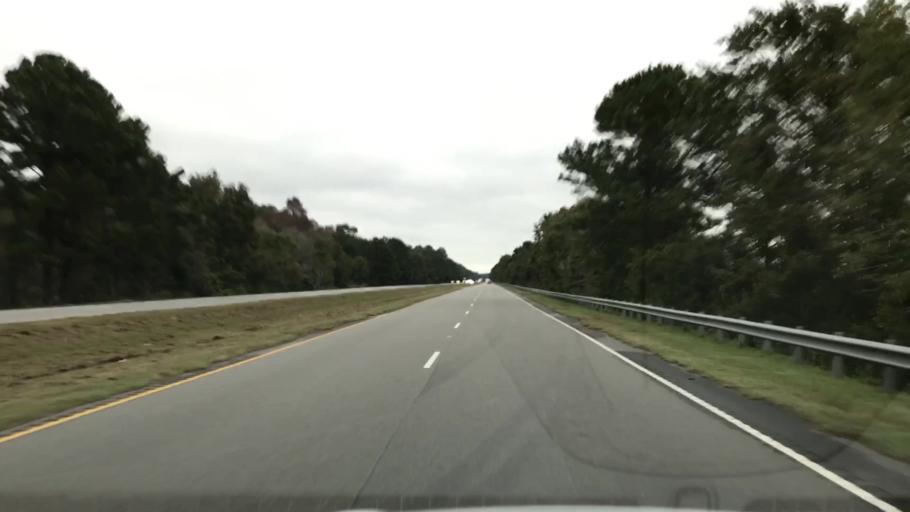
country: US
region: South Carolina
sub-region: Georgetown County
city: Georgetown
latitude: 33.1927
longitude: -79.3982
